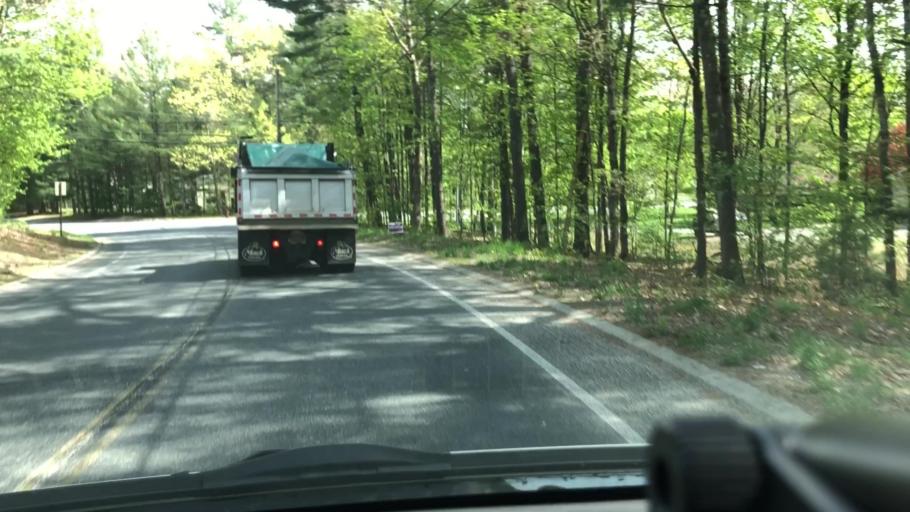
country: US
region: Massachusetts
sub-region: Hampshire County
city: Southampton
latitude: 42.2539
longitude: -72.7200
